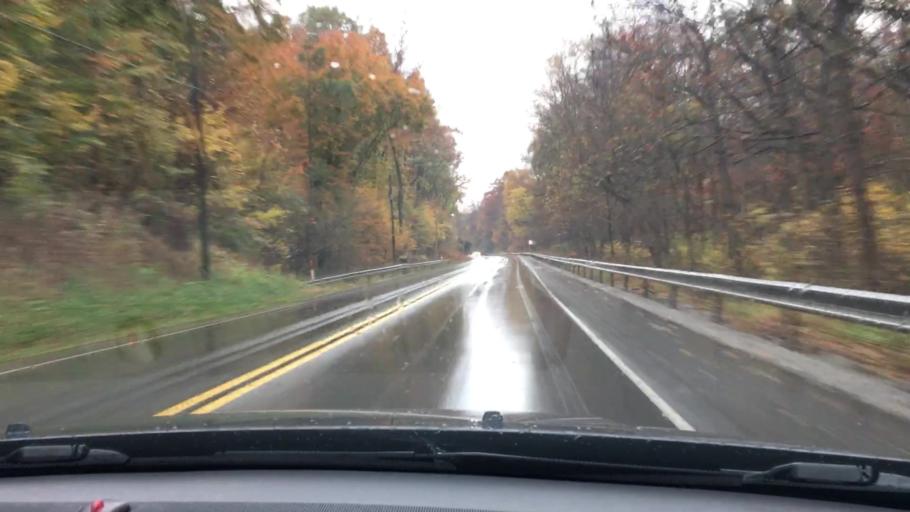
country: US
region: Pennsylvania
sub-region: York County
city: Susquehanna Trails
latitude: 39.8076
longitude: -76.3380
